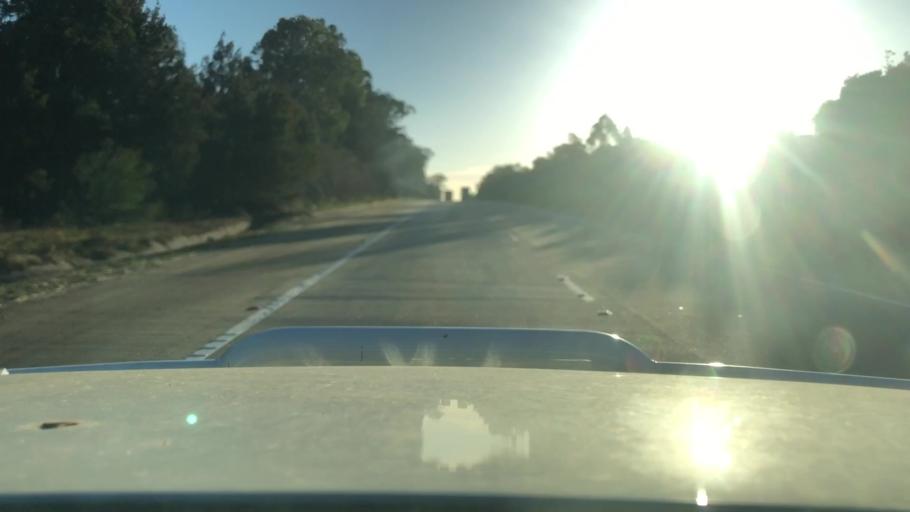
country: AU
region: New South Wales
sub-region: Wingecarribee
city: Bundanoon
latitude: -34.6815
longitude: 150.0539
